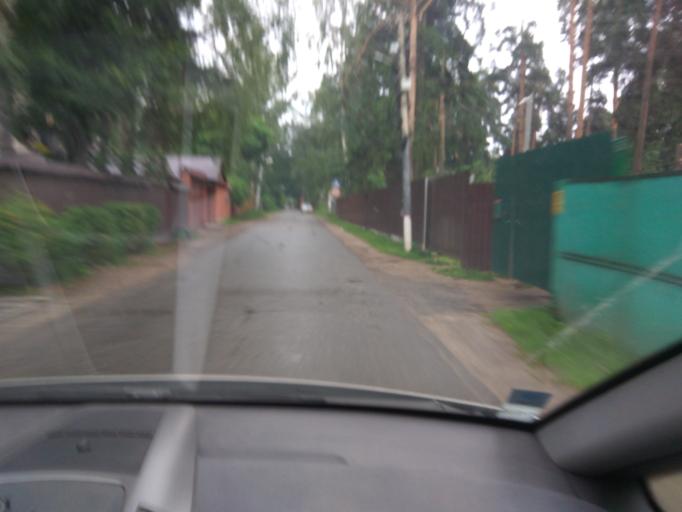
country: RU
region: Moskovskaya
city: Bykovo
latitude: 55.6280
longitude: 38.0770
